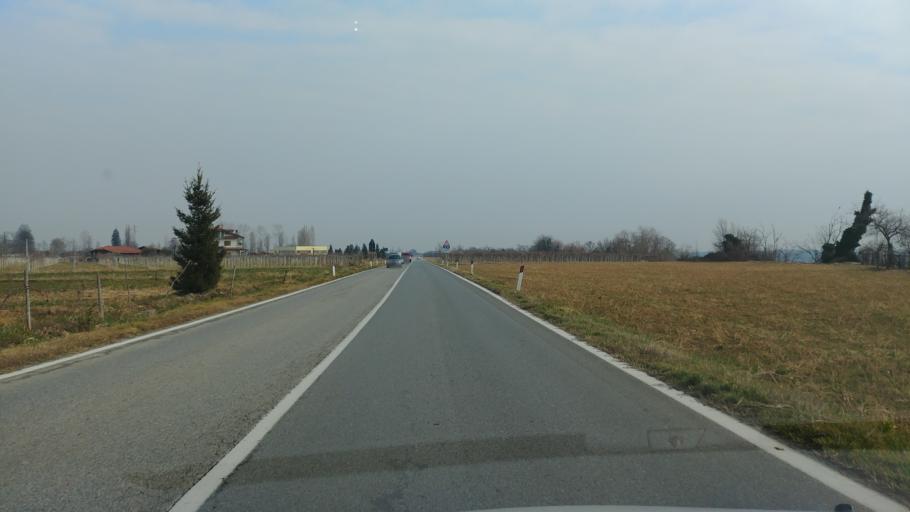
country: IT
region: Piedmont
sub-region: Provincia di Cuneo
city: Castelletto Stura
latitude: 44.4349
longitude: 7.5912
